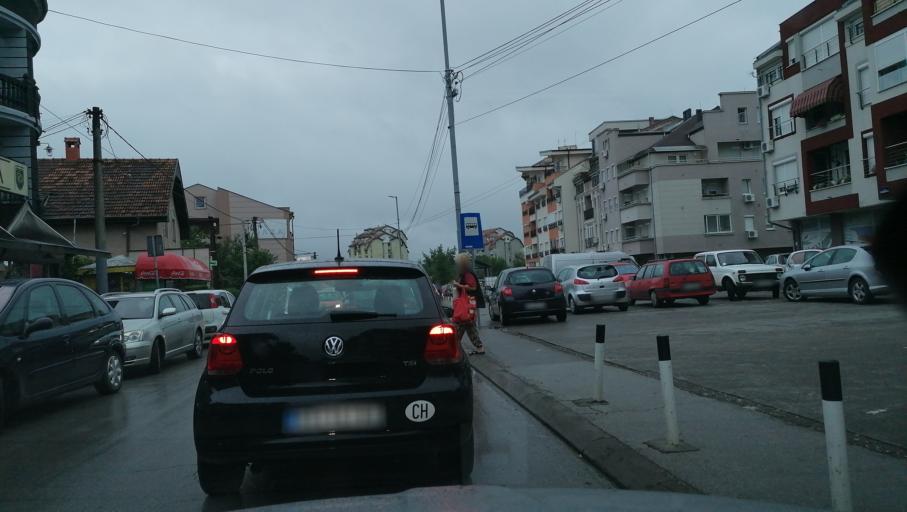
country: RS
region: Central Serbia
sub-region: Rasinski Okrug
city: Krusevac
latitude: 43.5697
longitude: 21.3298
